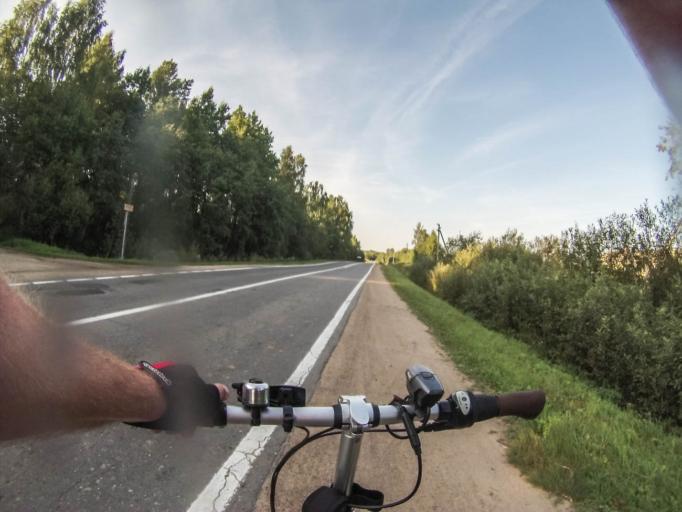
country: RU
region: Jaroslavl
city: Myshkin
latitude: 57.7496
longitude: 38.4364
